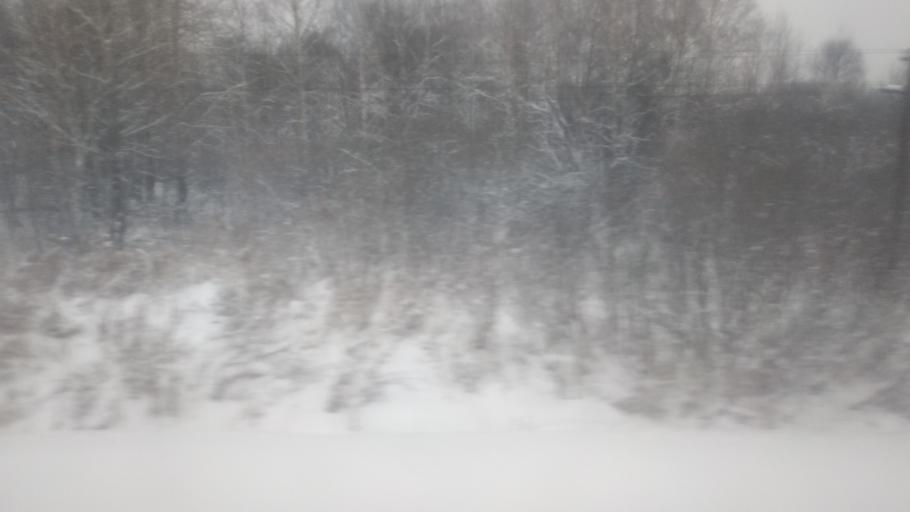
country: RU
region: Bashkortostan
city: Yanaul
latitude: 56.2526
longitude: 54.7048
